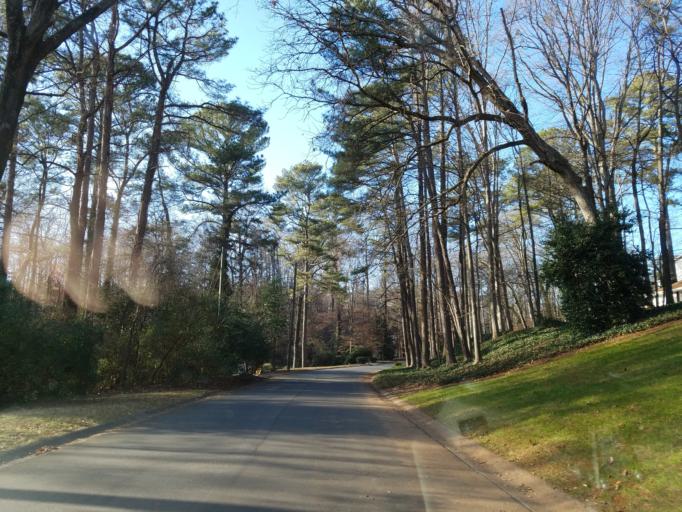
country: US
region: Georgia
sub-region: Cobb County
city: Vinings
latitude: 33.8543
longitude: -84.4865
